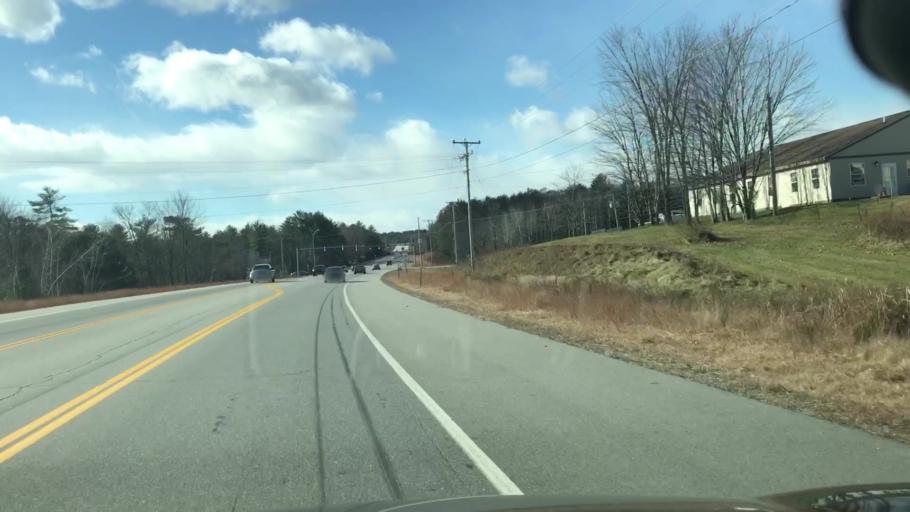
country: US
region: New Hampshire
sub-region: Merrimack County
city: Pittsfield
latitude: 43.3154
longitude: -71.3133
